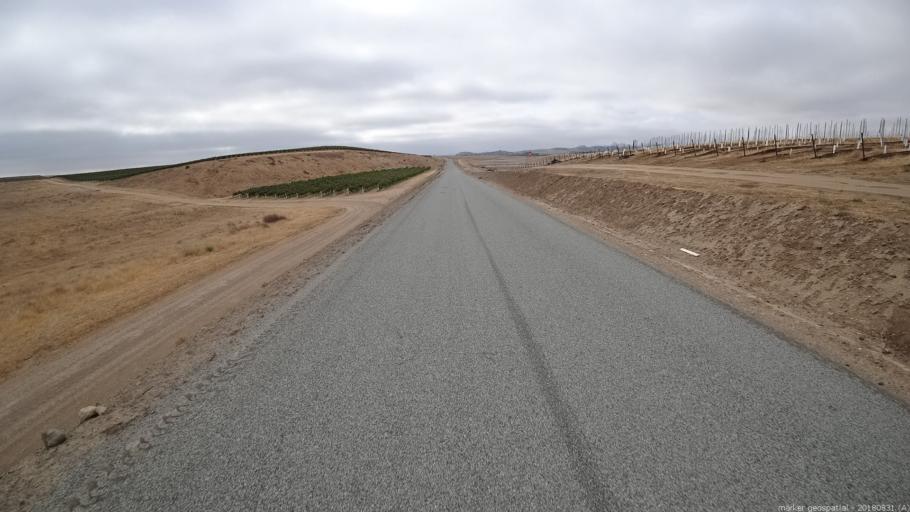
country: US
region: California
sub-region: Monterey County
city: King City
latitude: 36.1648
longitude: -121.1141
